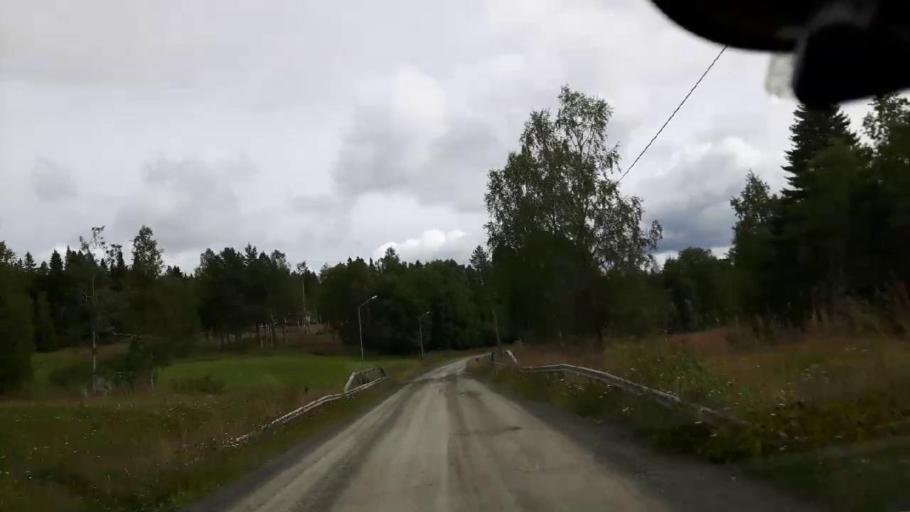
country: SE
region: Jaemtland
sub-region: Krokoms Kommun
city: Valla
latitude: 63.6739
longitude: 13.9453
